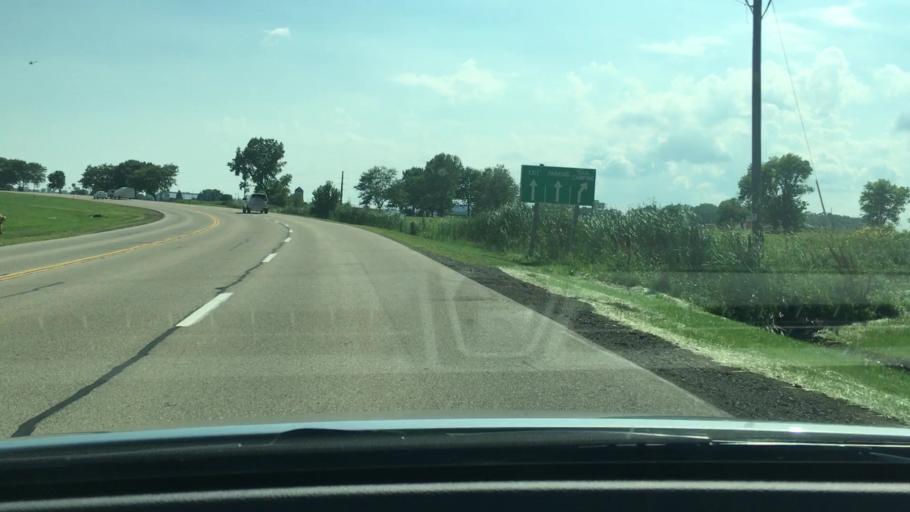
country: US
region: Wisconsin
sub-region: Winnebago County
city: Oshkosh
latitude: 43.9889
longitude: -88.5792
